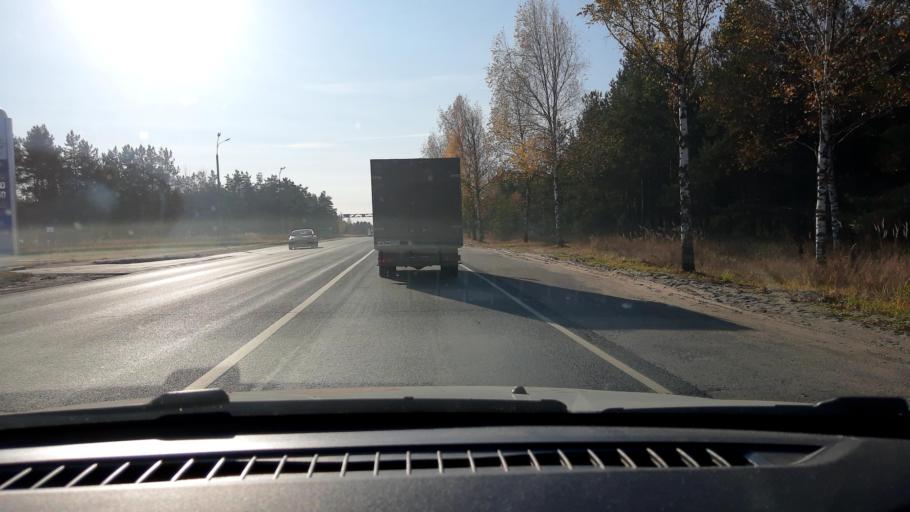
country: RU
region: Nizjnij Novgorod
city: Dzerzhinsk
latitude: 56.2935
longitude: 43.4760
